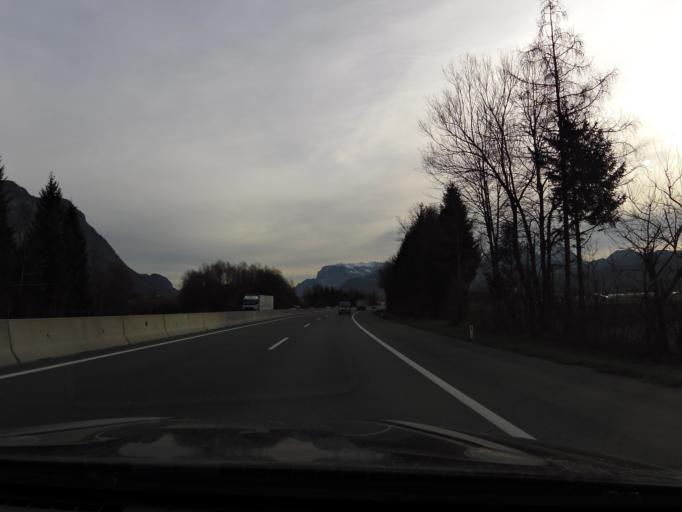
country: AT
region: Tyrol
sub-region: Politischer Bezirk Kufstein
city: Langkampfen
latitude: 47.5307
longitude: 12.0815
